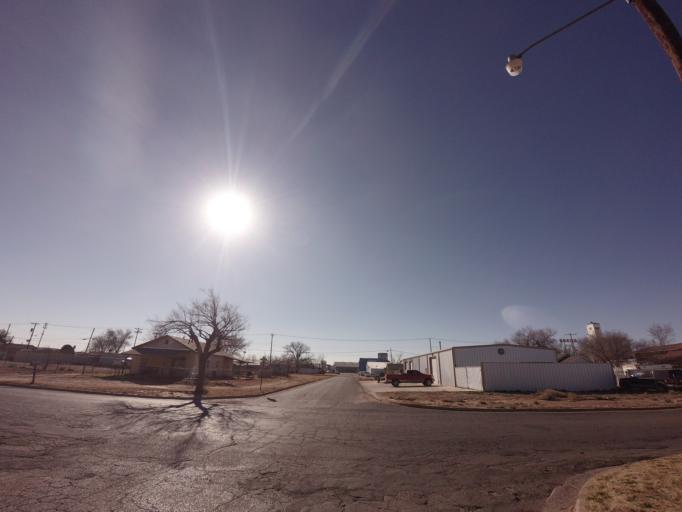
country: US
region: New Mexico
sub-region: Curry County
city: Clovis
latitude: 34.4009
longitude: -103.1953
